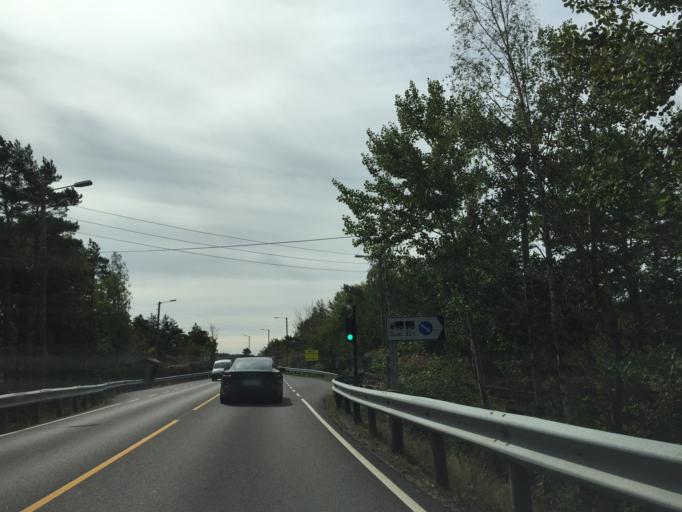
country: NO
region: Ostfold
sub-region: Fredrikstad
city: Fredrikstad
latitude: 59.1496
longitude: 10.9408
